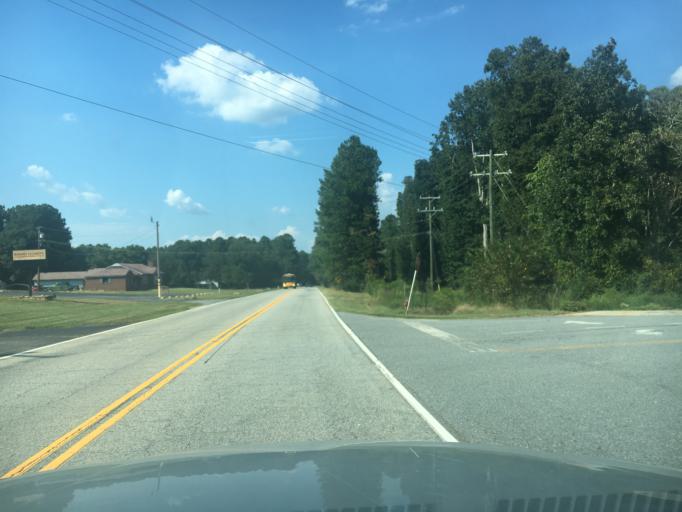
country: US
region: South Carolina
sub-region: Anderson County
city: Pendleton
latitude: 34.5504
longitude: -82.8091
